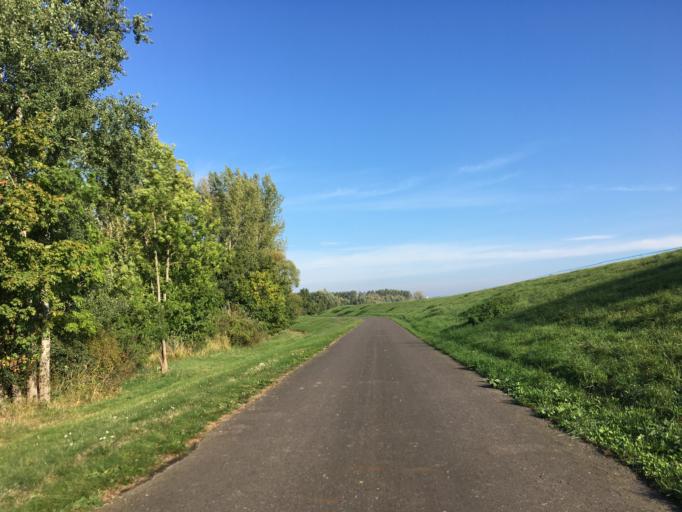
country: DE
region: Brandenburg
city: Reitwein
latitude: 52.5262
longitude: 14.6023
